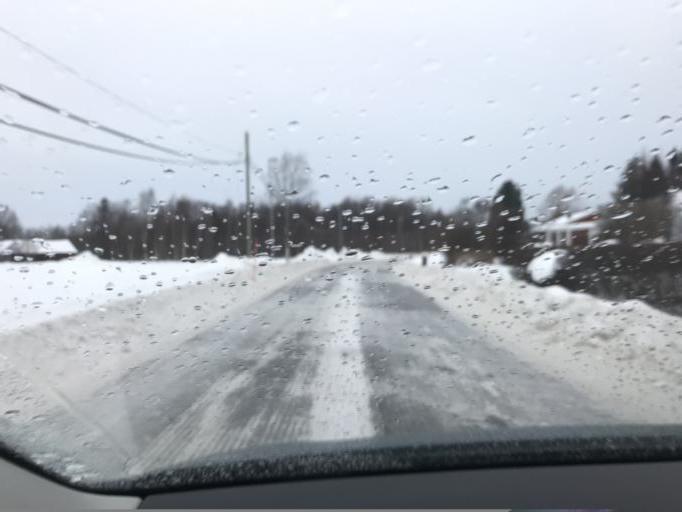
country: SE
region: Norrbotten
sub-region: Lulea Kommun
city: Sodra Sunderbyn
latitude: 65.6604
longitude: 21.9327
